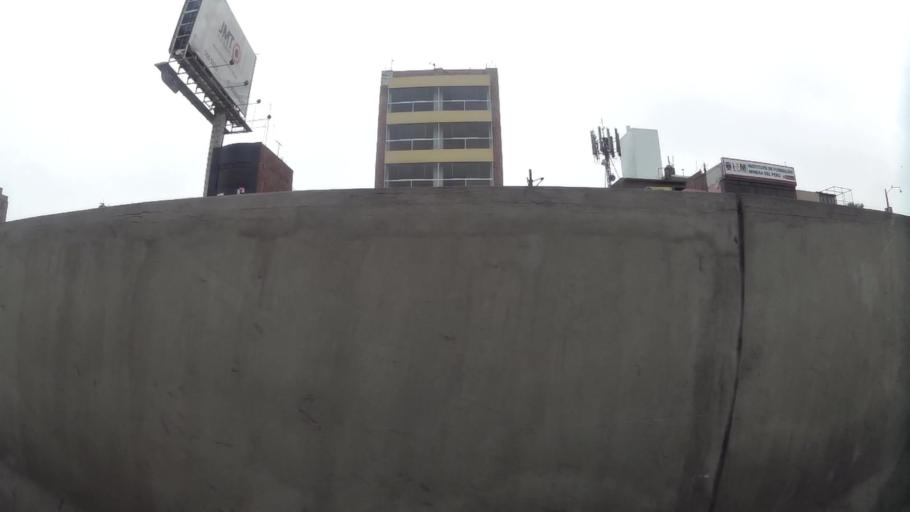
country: PE
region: Lima
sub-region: Lima
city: Independencia
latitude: -11.9995
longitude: -77.0627
